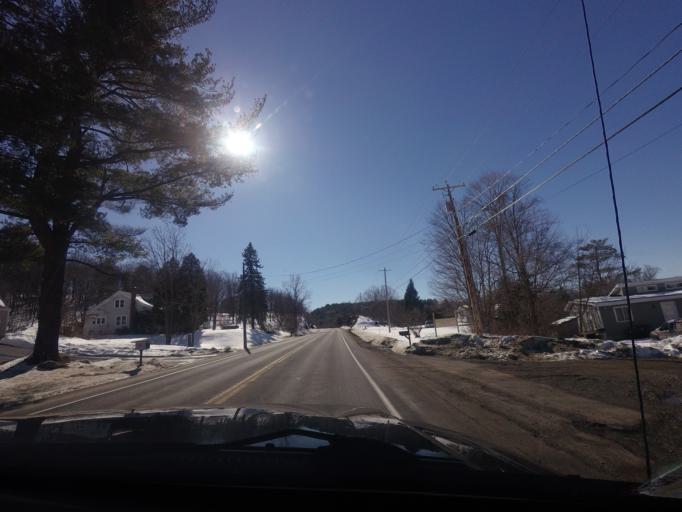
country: US
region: New York
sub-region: Saratoga County
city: Waterford
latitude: 42.8281
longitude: -73.6276
